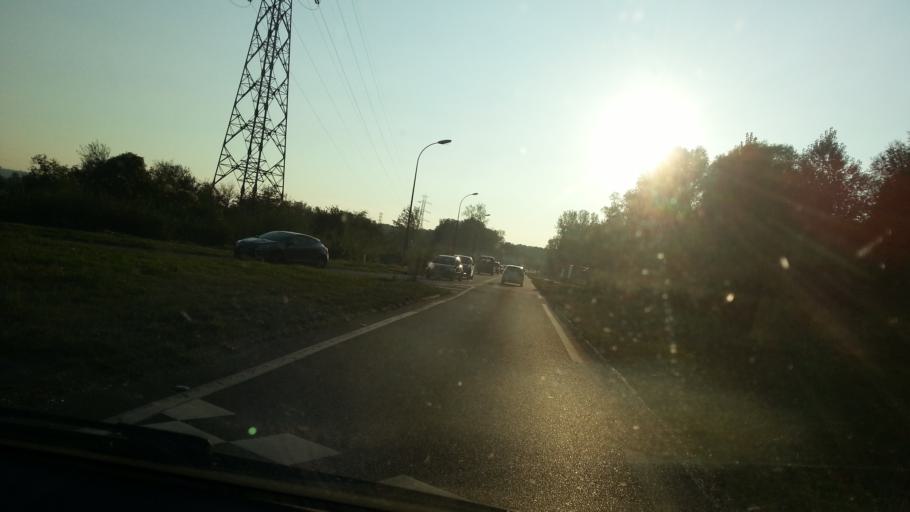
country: FR
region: Picardie
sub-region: Departement de l'Oise
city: Les Ageux
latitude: 49.3243
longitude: 2.6025
